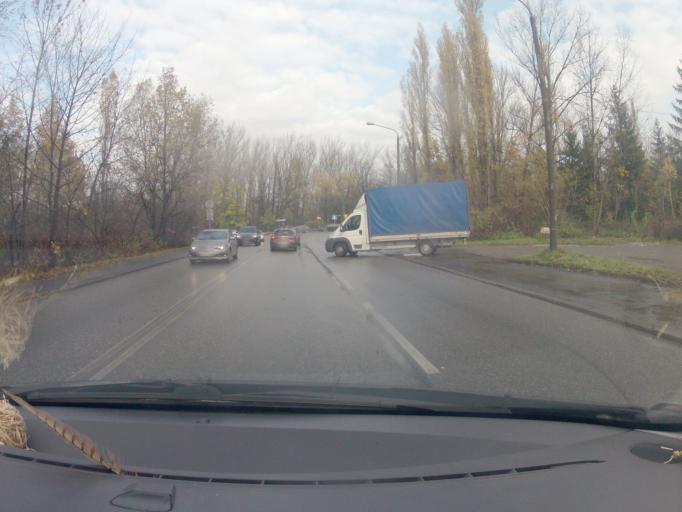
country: PL
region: Lesser Poland Voivodeship
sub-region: Powiat wielicki
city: Kokotow
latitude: 50.0782
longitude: 20.0627
